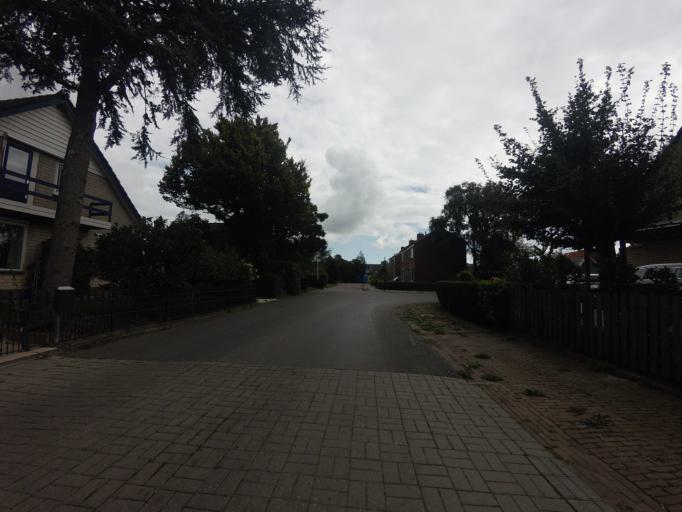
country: NL
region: Friesland
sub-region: Sudwest Fryslan
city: IJlst
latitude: 52.9964
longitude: 5.6483
